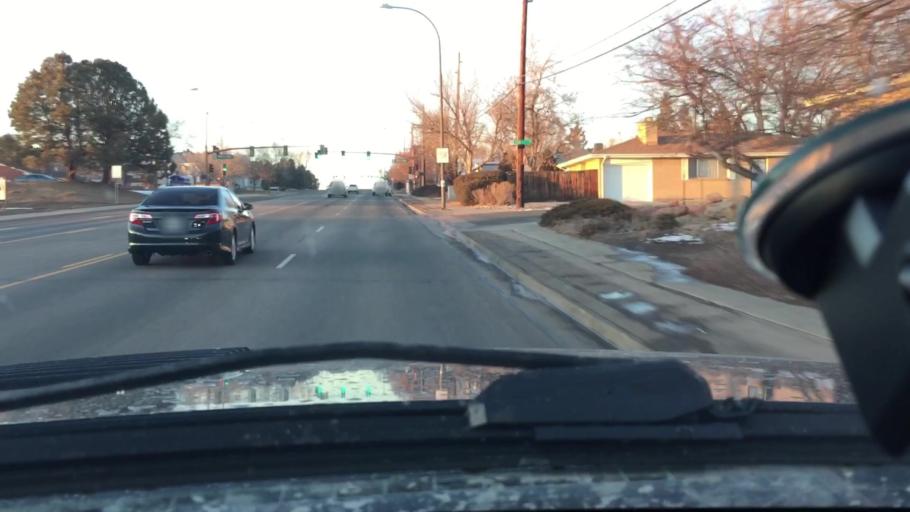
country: US
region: Colorado
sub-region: Adams County
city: Federal Heights
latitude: 39.8520
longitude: -104.9966
